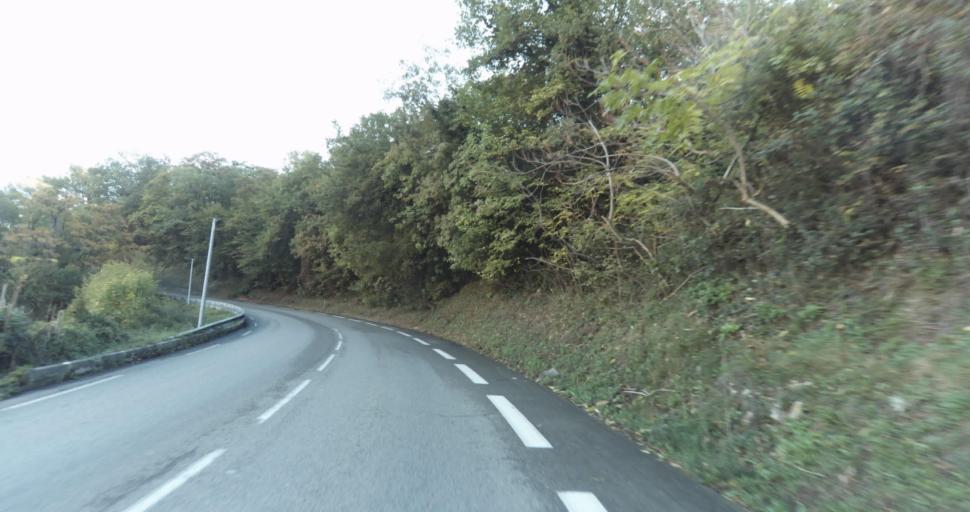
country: FR
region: Provence-Alpes-Cote d'Azur
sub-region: Departement des Alpes-Maritimes
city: Saint-Jeannet
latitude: 43.7438
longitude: 7.1311
